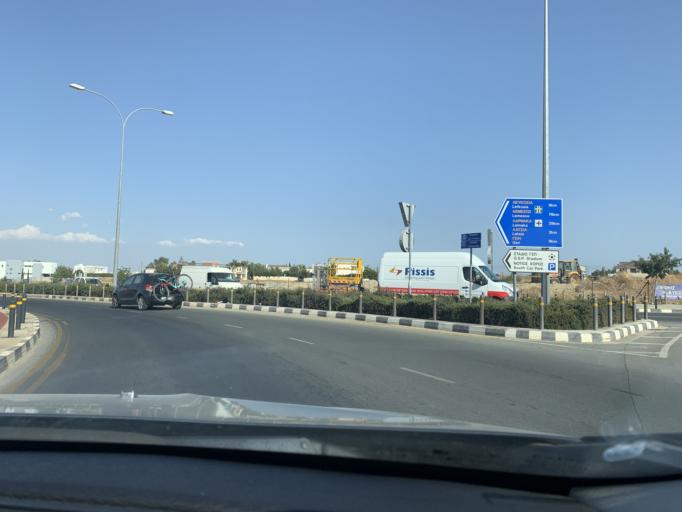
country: CY
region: Lefkosia
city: Tseri
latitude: 35.1117
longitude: 33.3553
